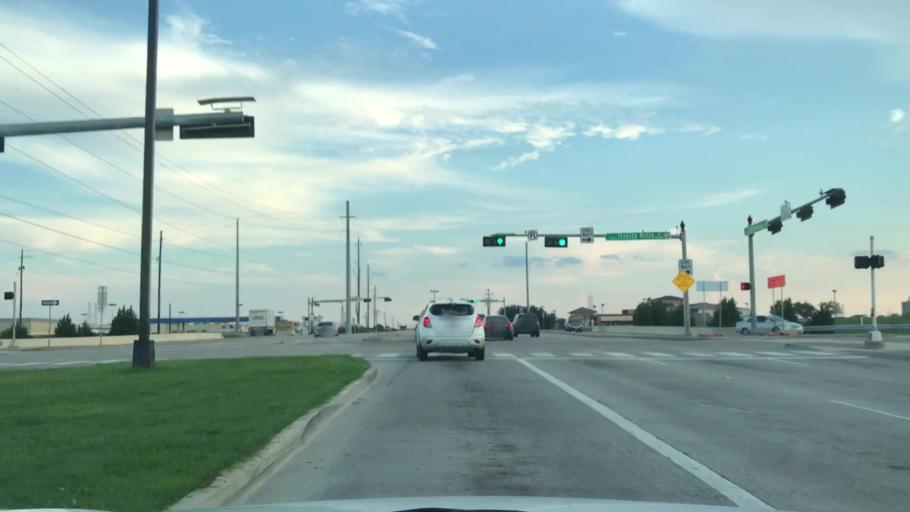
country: US
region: Texas
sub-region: Dallas County
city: Carrollton
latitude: 32.9841
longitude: -96.9099
